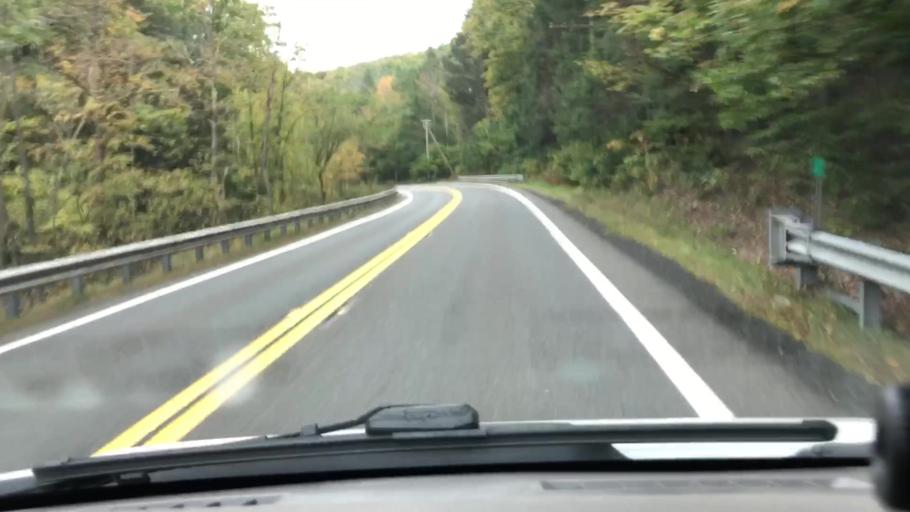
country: US
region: Massachusetts
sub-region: Hampshire County
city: Chesterfield
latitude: 42.3373
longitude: -72.8854
